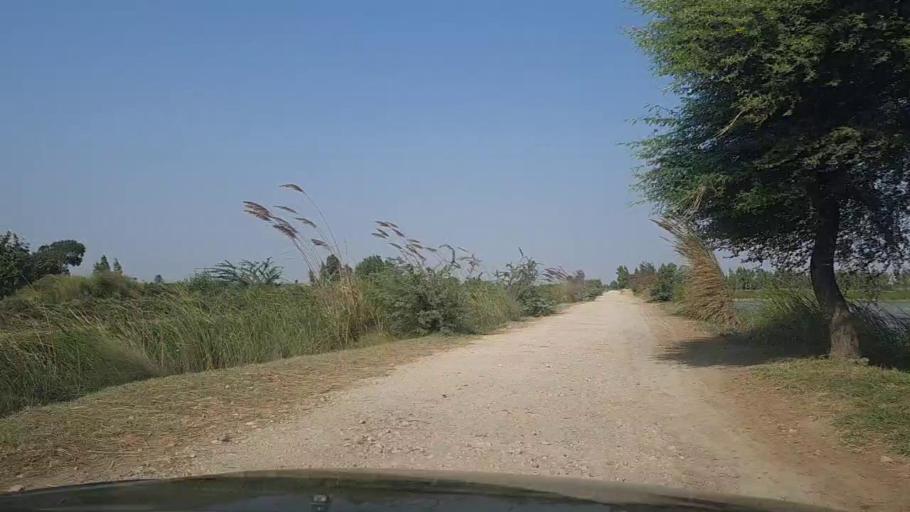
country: PK
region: Sindh
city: Thatta
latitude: 24.6197
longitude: 67.8157
